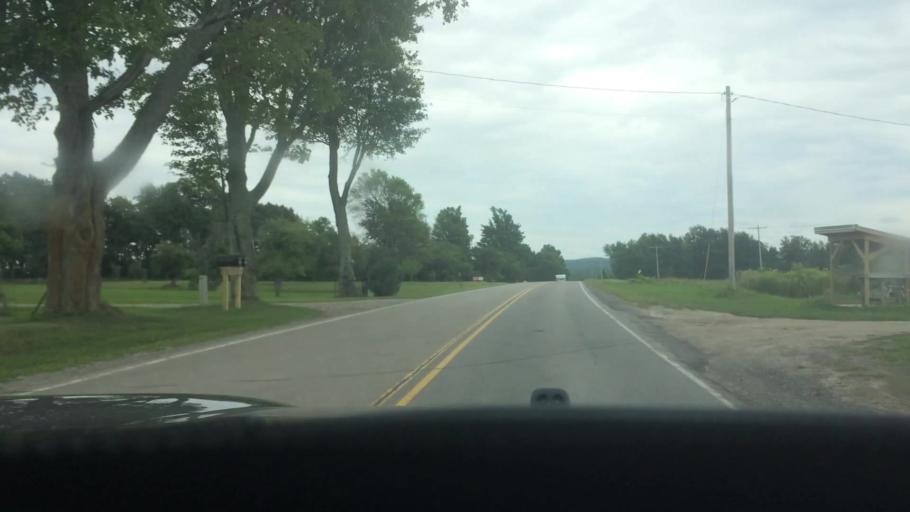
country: US
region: New York
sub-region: St. Lawrence County
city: Canton
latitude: 44.5417
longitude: -75.0860
